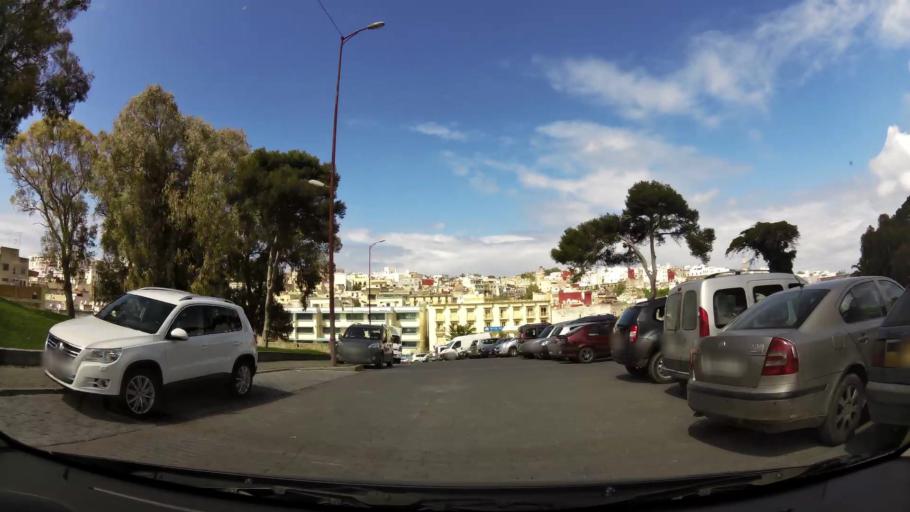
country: MA
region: Tanger-Tetouan
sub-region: Tanger-Assilah
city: Tangier
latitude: 35.7848
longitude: -5.8147
